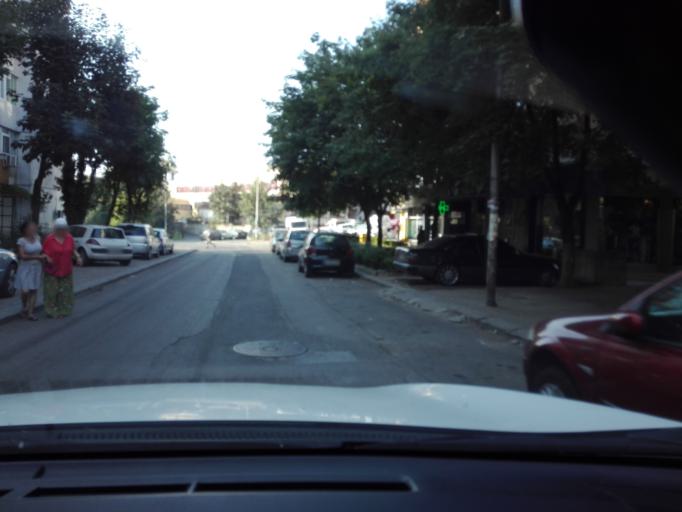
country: BG
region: Burgas
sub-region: Obshtina Burgas
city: Burgas
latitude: 42.4621
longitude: 27.4148
